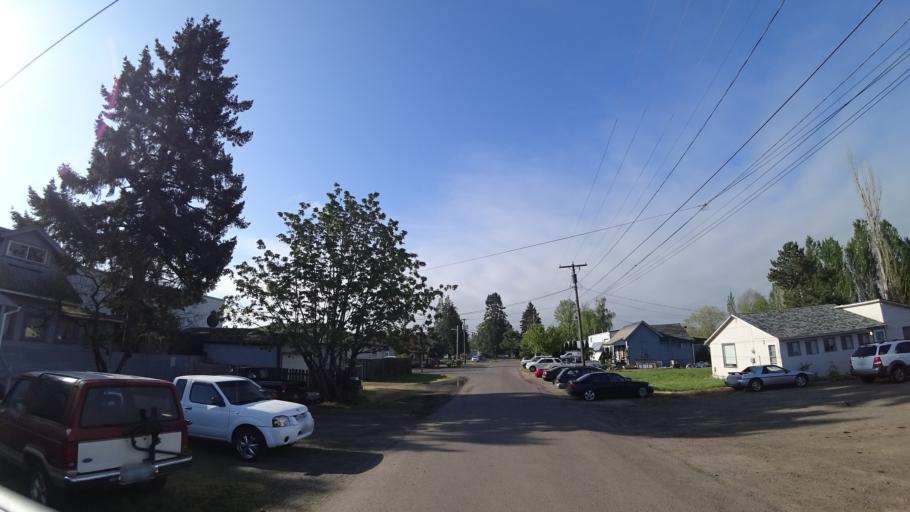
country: US
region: Oregon
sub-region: Washington County
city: Hillsboro
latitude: 45.5148
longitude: -122.9925
